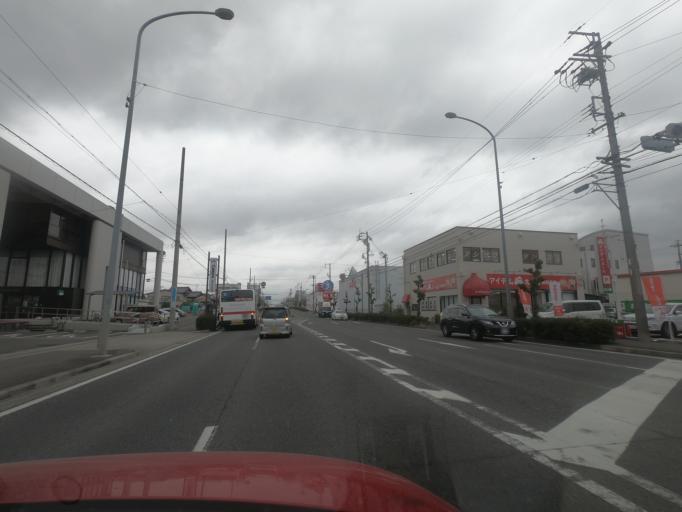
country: JP
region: Aichi
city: Kasugai
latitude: 35.2510
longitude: 136.9718
